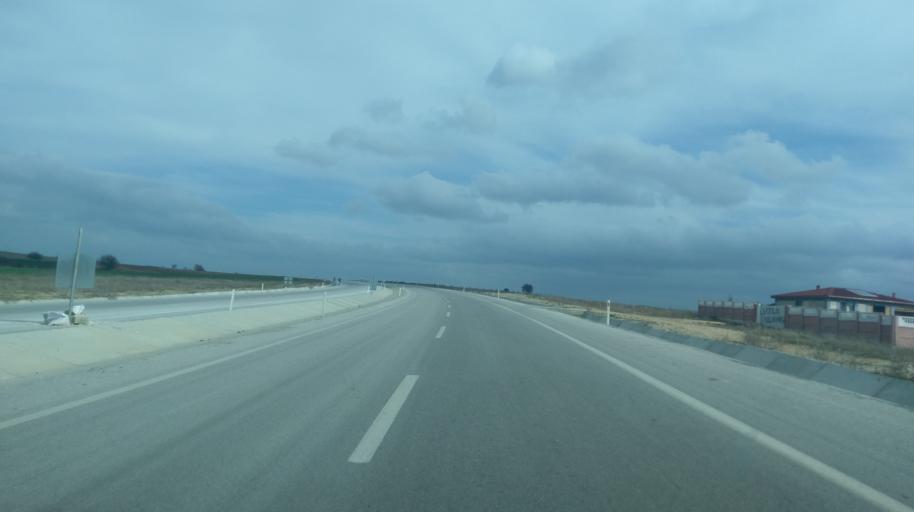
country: TR
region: Kirklareli
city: Inece
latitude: 41.6803
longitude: 27.0997
